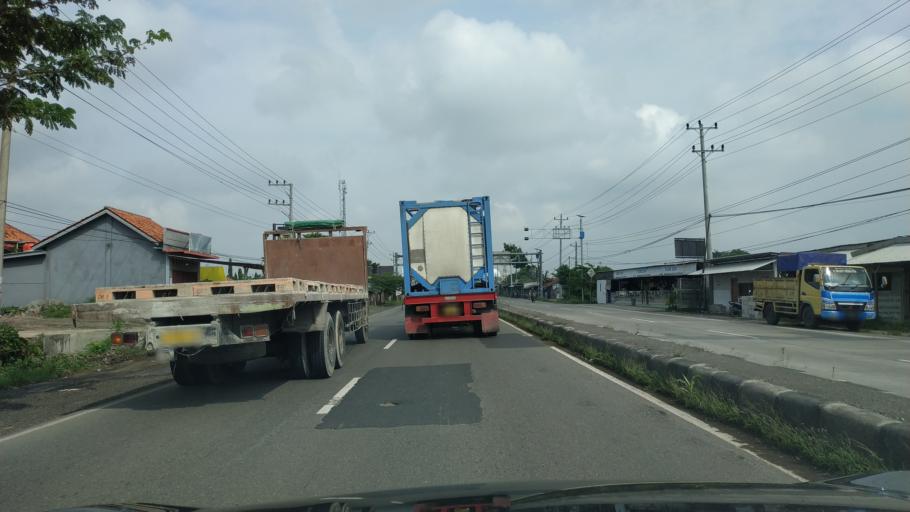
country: ID
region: Central Java
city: Bulakamba
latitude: -6.8749
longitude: 108.9272
